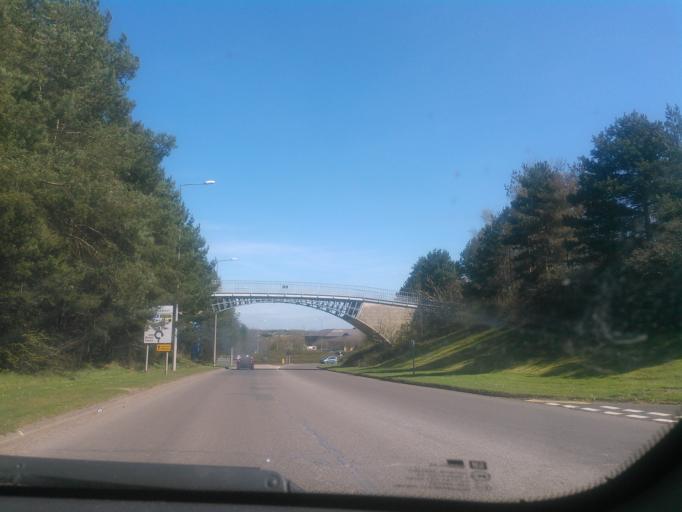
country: GB
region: England
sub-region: Telford and Wrekin
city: Telford
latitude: 52.6784
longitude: -2.4537
